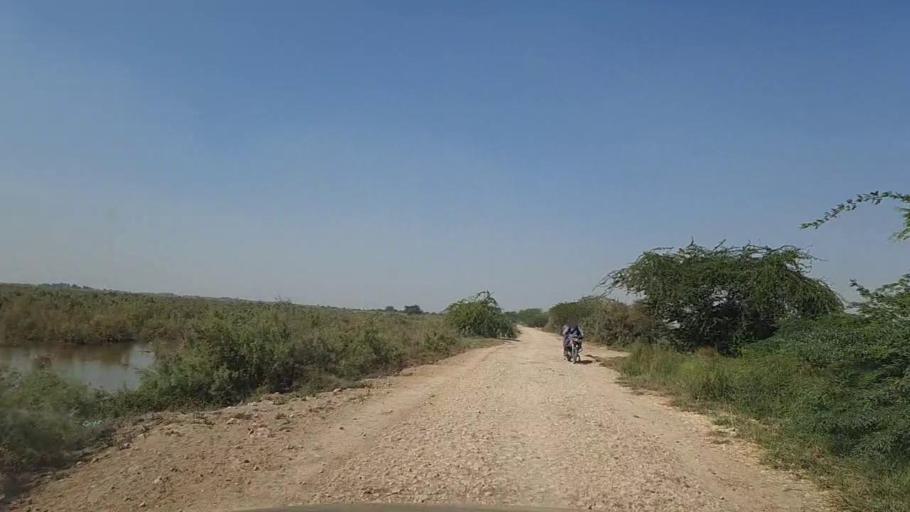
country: PK
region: Sindh
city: Daro Mehar
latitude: 24.8270
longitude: 68.1480
